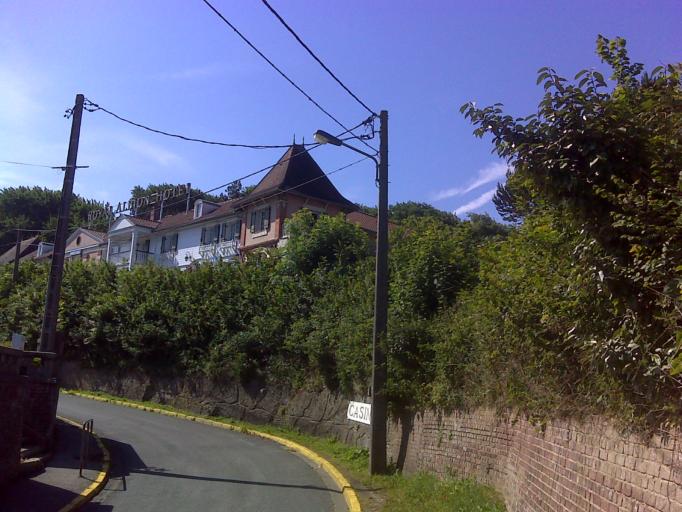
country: FR
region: Haute-Normandie
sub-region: Departement de la Seine-Maritime
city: Criel-sur-Mer
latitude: 50.0443
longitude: 1.3301
